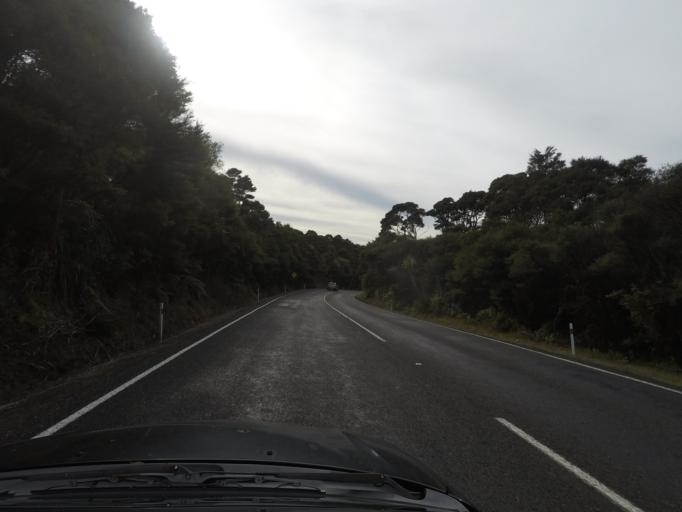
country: NZ
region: Auckland
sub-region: Auckland
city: Titirangi
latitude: -36.9390
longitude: 174.5547
